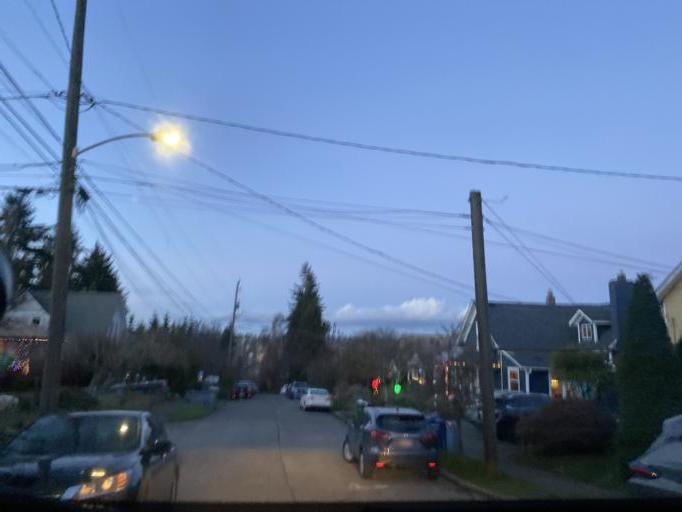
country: US
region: Washington
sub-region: King County
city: Seattle
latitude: 47.6599
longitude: -122.3949
